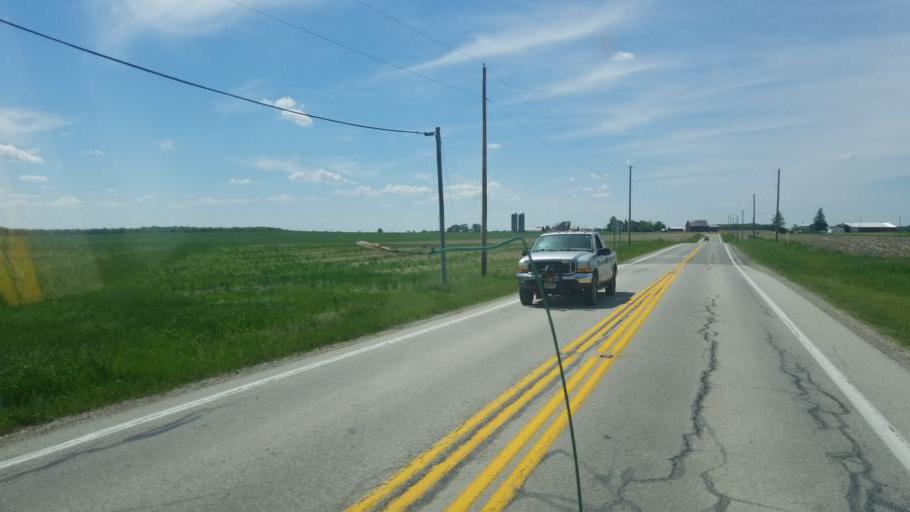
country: US
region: Ohio
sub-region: Sandusky County
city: Mount Carmel
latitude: 41.0784
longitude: -82.9221
